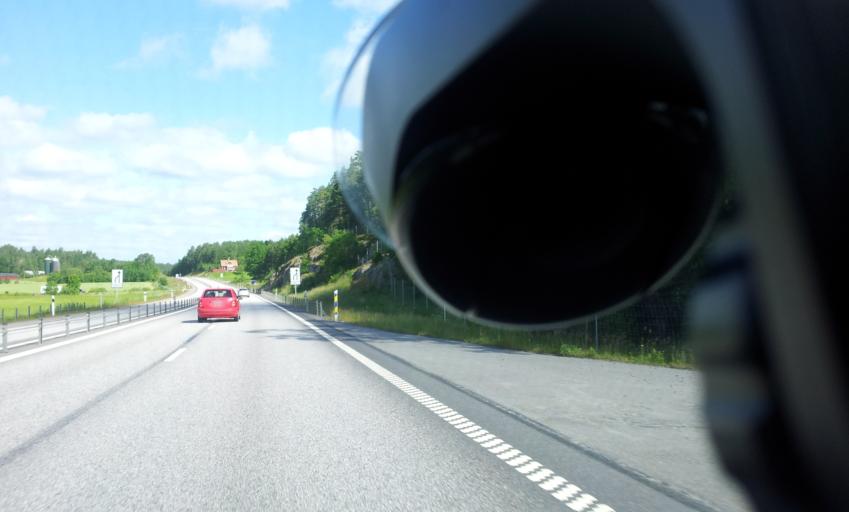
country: SE
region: OEstergoetland
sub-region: Soderkopings Kommun
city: Soederkoeping
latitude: 58.4174
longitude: 16.3980
